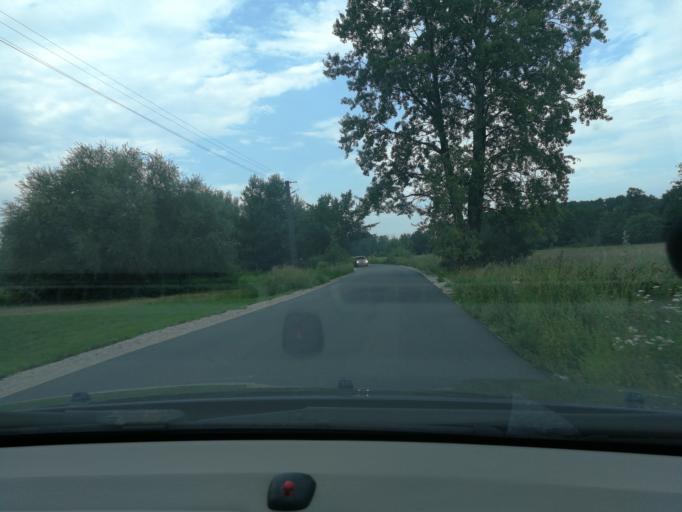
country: PL
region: Masovian Voivodeship
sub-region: Powiat warszawski zachodni
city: Bieniewice
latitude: 52.1082
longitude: 20.5550
